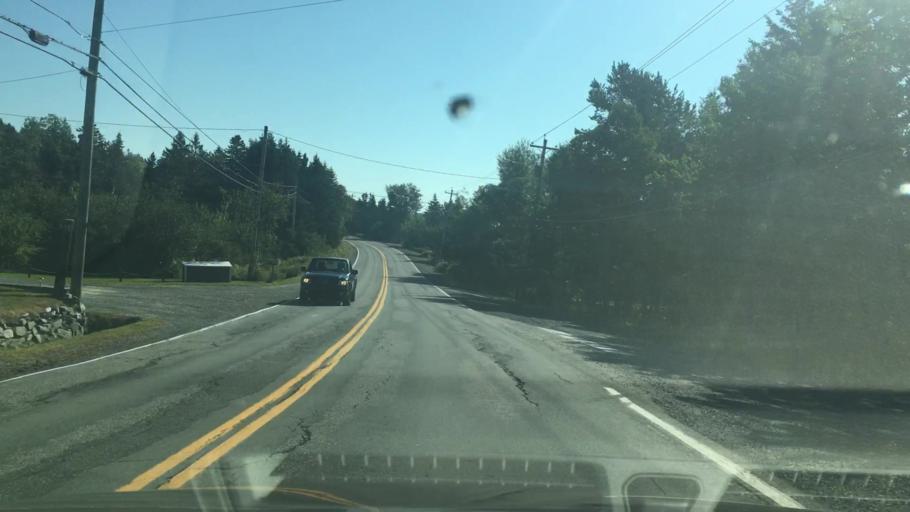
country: CA
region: Nova Scotia
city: Cole Harbour
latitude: 44.7766
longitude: -63.0712
